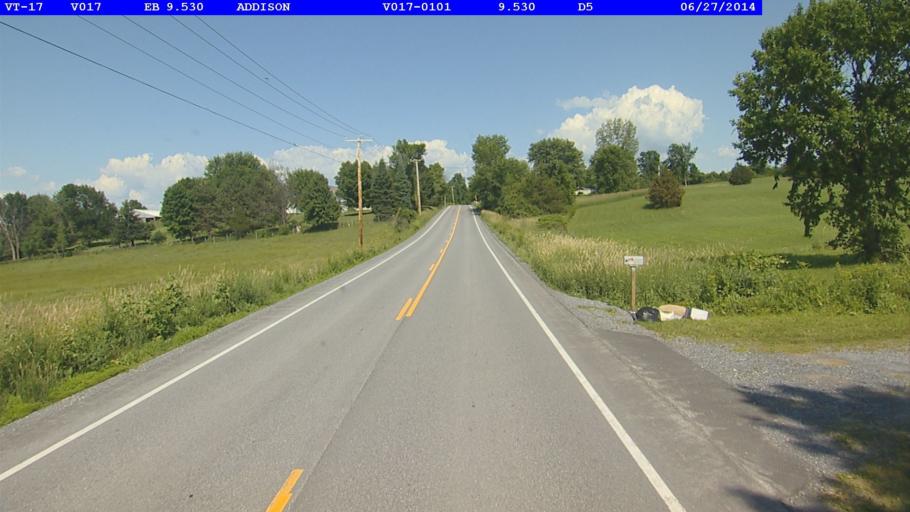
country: US
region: Vermont
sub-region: Addison County
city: Vergennes
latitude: 44.0852
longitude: -73.2806
